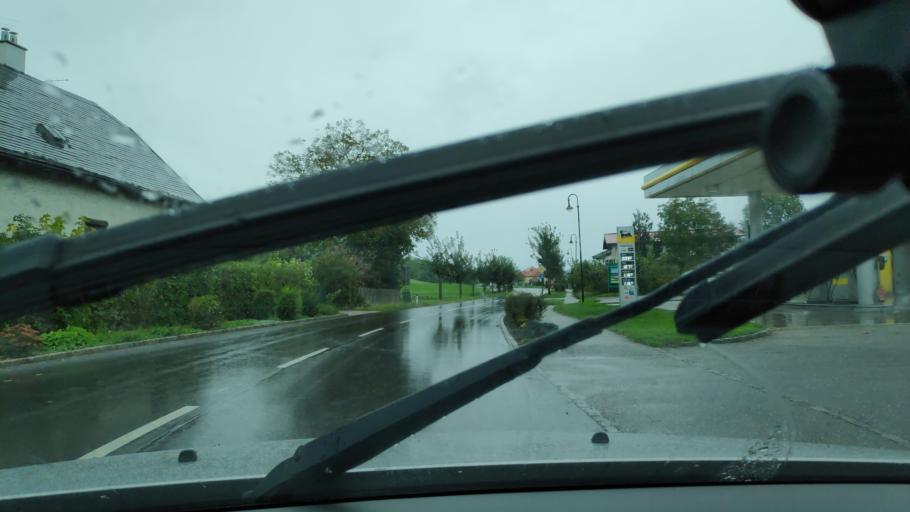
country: AT
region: Lower Austria
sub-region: Politischer Bezirk Neunkirchen
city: Grunbach am Schneeberg
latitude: 47.7969
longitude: 15.9934
